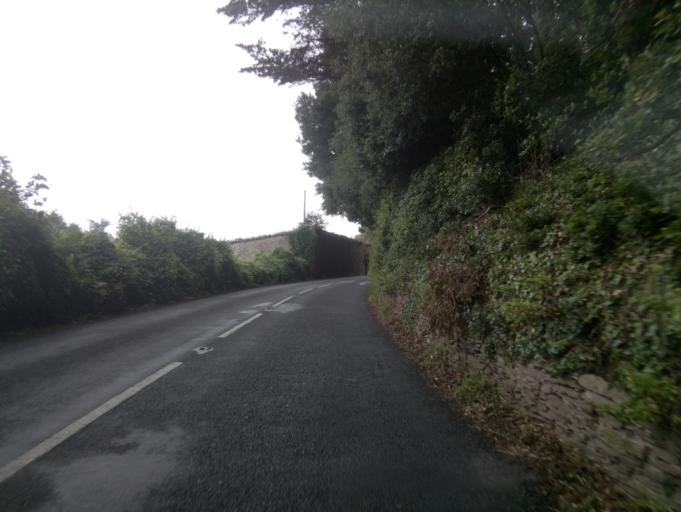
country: GB
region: England
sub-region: Devon
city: Dartmouth
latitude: 50.2983
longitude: -3.6390
